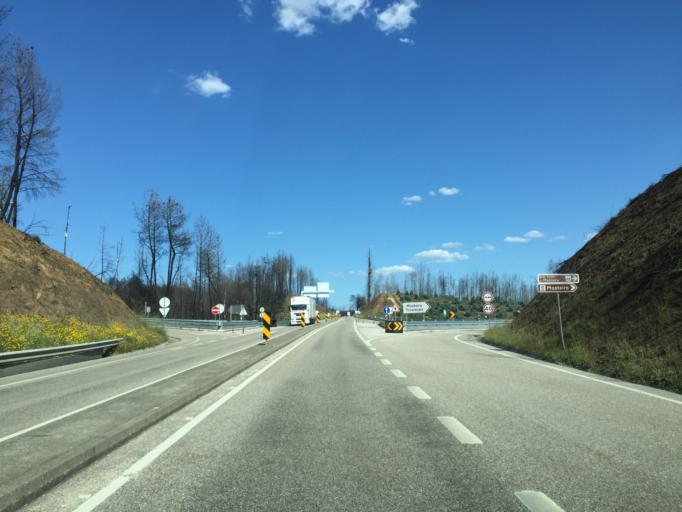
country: PT
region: Leiria
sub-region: Pedrogao Grande
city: Pedrogao Grande
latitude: 39.9277
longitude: -8.1817
